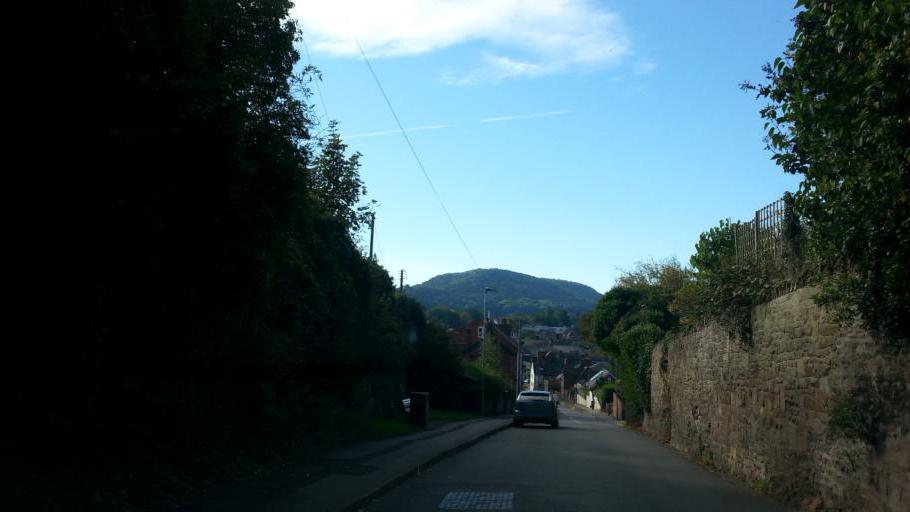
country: GB
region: England
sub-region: Herefordshire
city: Ross on Wye
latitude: 51.9194
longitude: -2.5812
